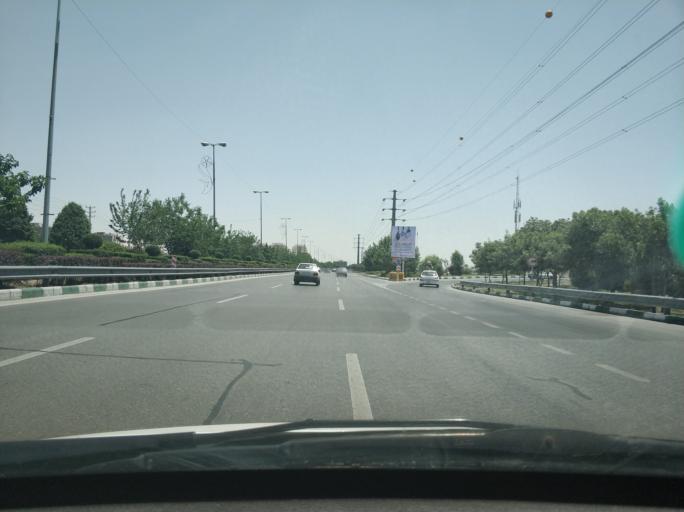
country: IR
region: Razavi Khorasan
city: Mashhad
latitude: 36.3465
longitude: 59.4852
